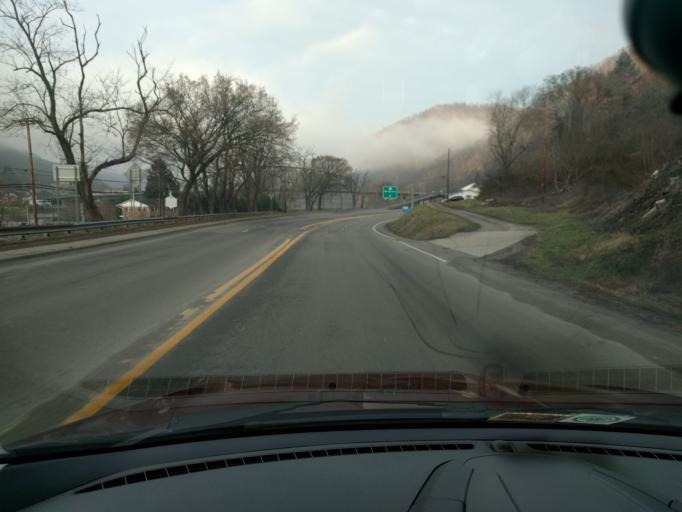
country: US
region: West Virginia
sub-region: Kanawha County
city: Montgomery
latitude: 38.1830
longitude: -81.3116
